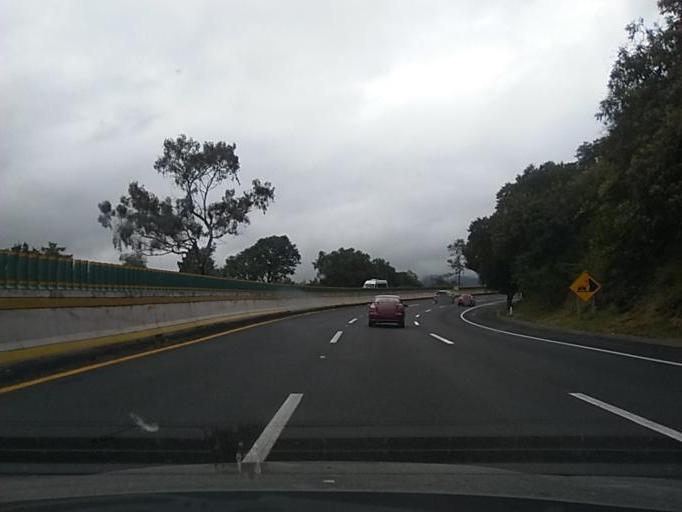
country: MX
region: Mexico City
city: Xochimilco
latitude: 19.2186
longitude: -99.1308
